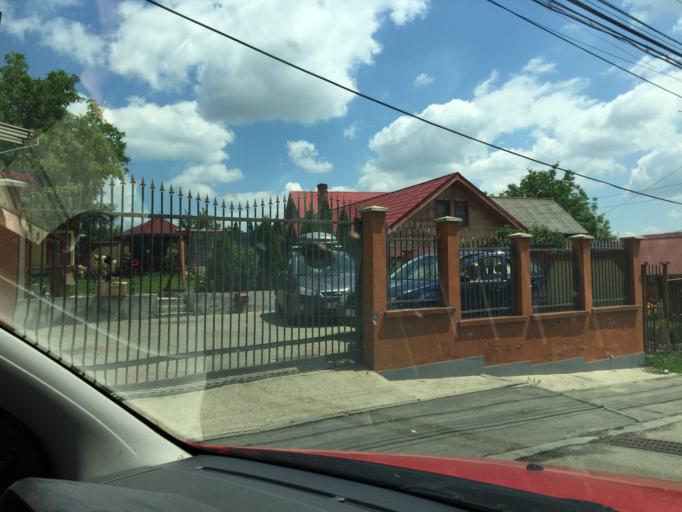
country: RO
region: Cluj
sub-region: Municipiul Cluj-Napoca
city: Cluj-Napoca
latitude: 46.7921
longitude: 23.5757
